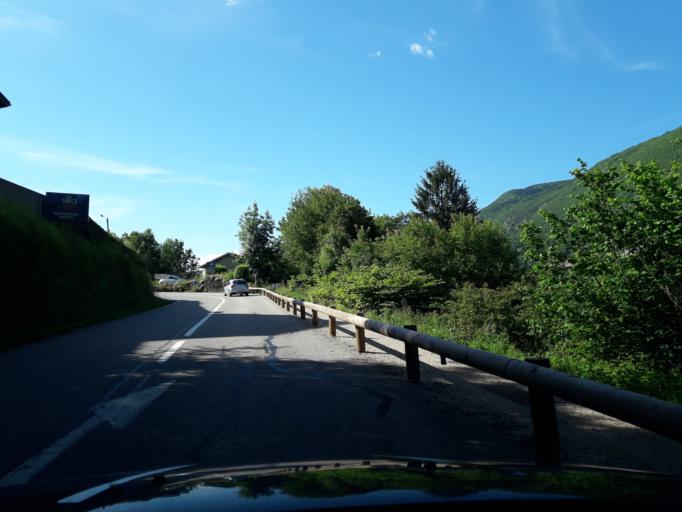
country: FR
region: Rhone-Alpes
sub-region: Departement de la Savoie
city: Novalaise
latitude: 45.5601
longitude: 5.8075
